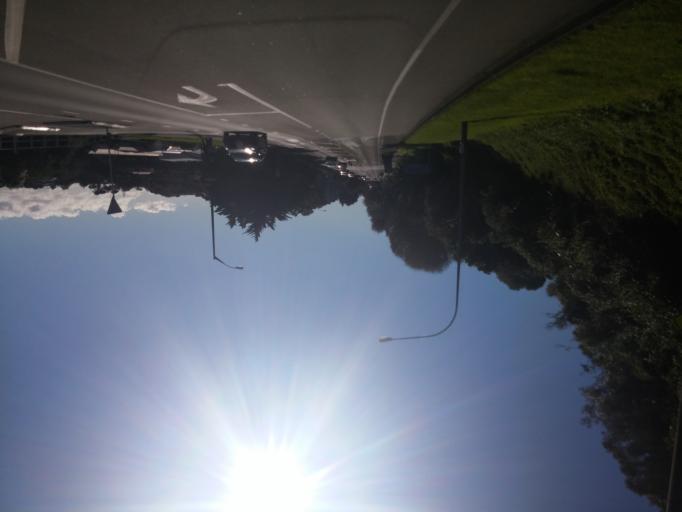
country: NZ
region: Wellington
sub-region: Wellington City
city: Wellington
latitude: -41.2374
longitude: 174.7980
